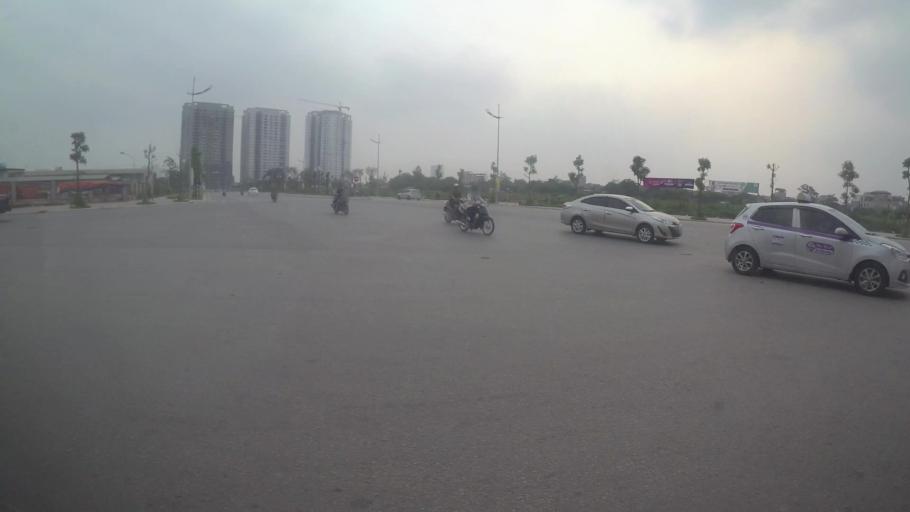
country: VN
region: Ha Noi
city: Cau Dien
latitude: 21.0519
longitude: 105.7361
